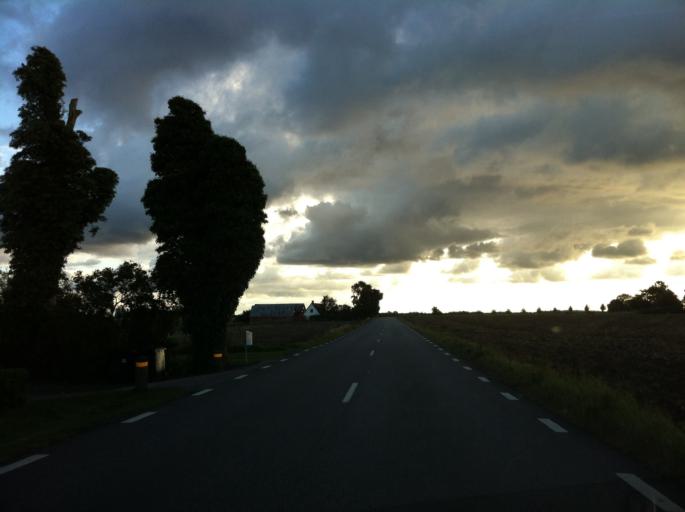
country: SE
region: Skane
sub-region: Svalovs Kommun
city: Svaloev
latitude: 55.8870
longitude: 13.1746
